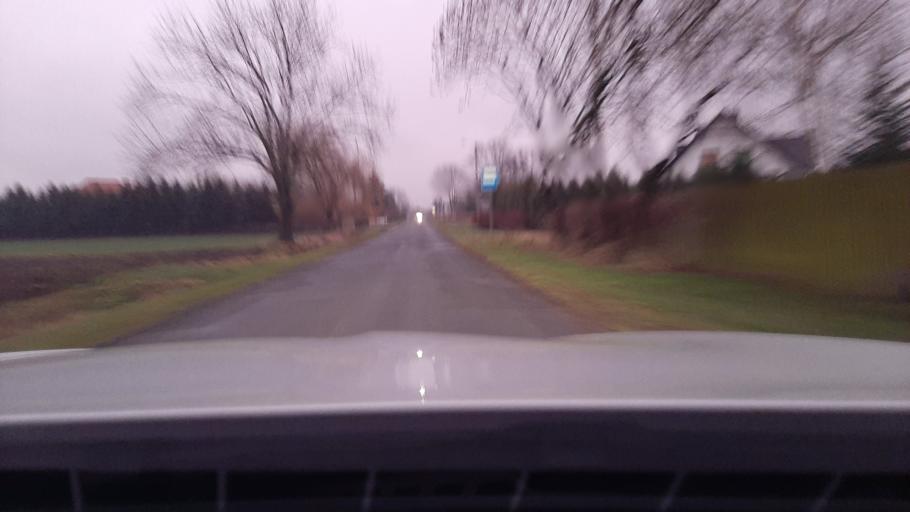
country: PL
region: Lublin Voivodeship
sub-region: Powiat lubelski
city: Garbow
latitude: 51.3528
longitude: 22.3904
